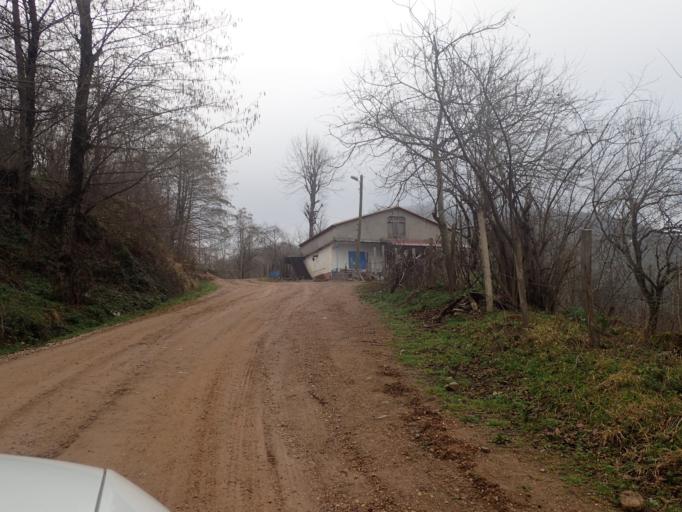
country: TR
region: Ordu
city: Camas
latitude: 40.9108
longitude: 37.5651
